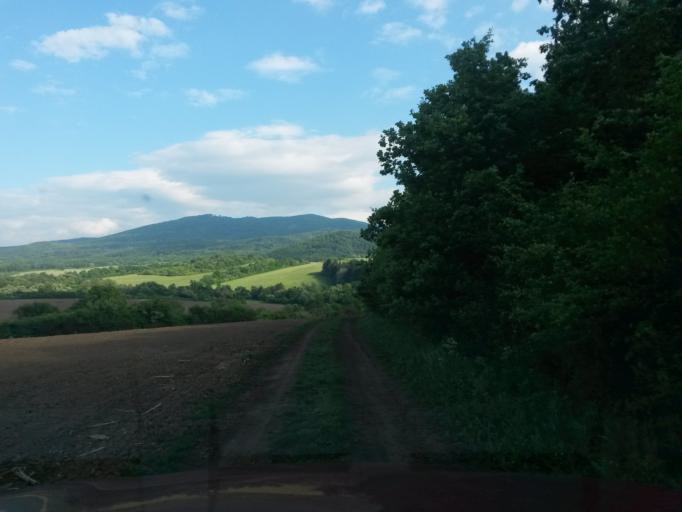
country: SK
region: Kosicky
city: Secovce
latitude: 48.7430
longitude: 21.4681
